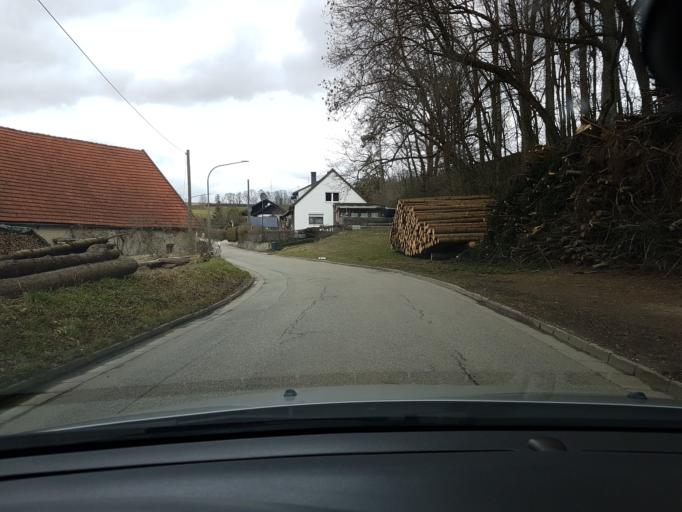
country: DE
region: Bavaria
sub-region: Lower Bavaria
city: Landshut
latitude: 48.5199
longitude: 12.1769
